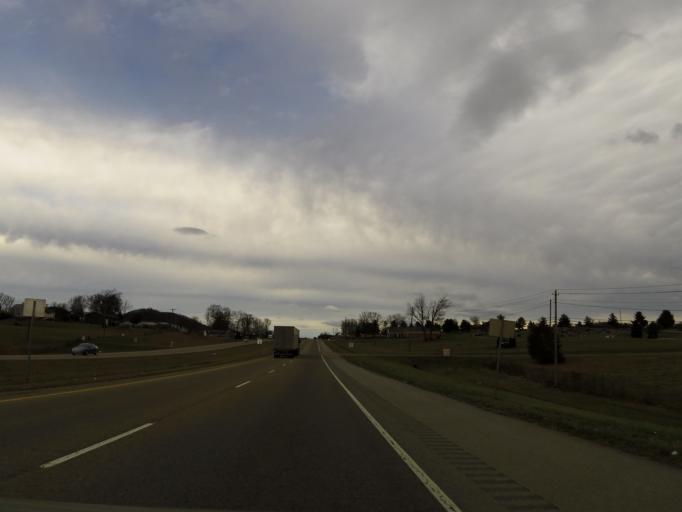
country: US
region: Tennessee
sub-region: Greene County
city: Tusculum
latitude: 36.1968
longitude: -82.7234
